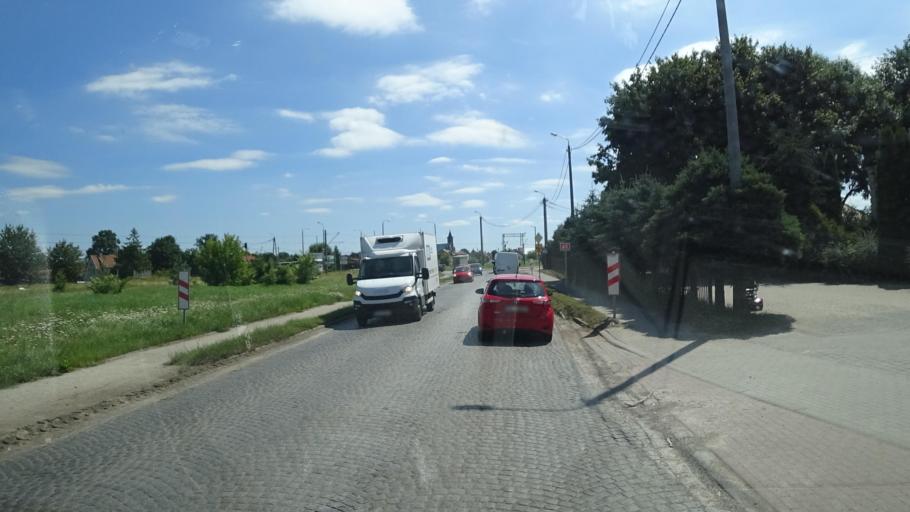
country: PL
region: Warmian-Masurian Voivodeship
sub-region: Powiat elcki
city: Prostki
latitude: 53.7017
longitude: 22.4259
